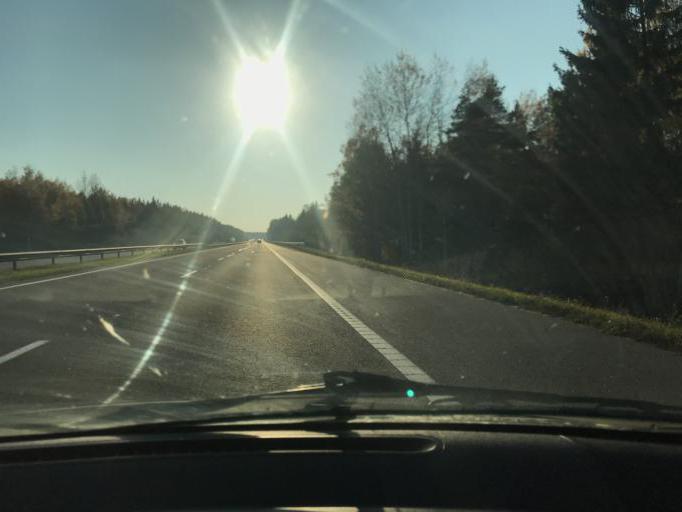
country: BY
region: Minsk
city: Loshnitsa
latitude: 54.2818
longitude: 28.7362
